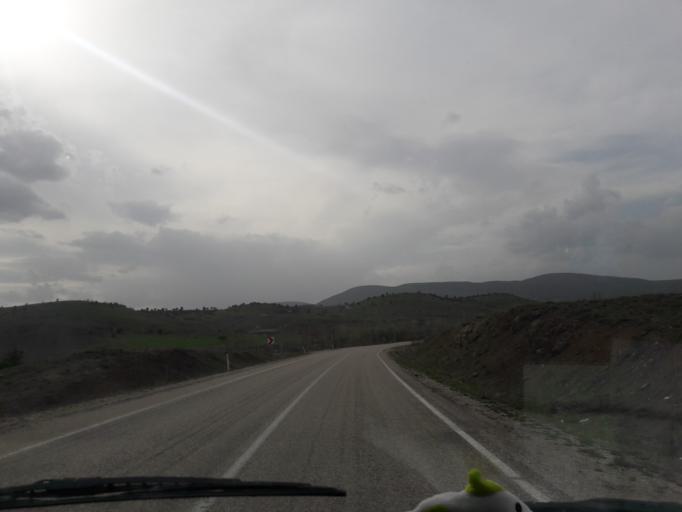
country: TR
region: Gumushane
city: Siran
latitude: 40.1610
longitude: 39.0121
